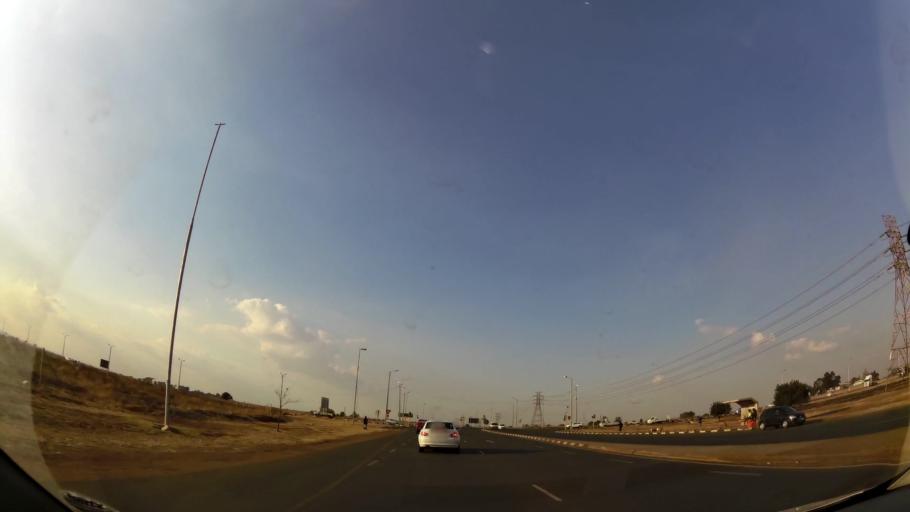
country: ZA
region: Gauteng
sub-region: Ekurhuleni Metropolitan Municipality
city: Germiston
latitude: -26.3348
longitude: 28.2311
